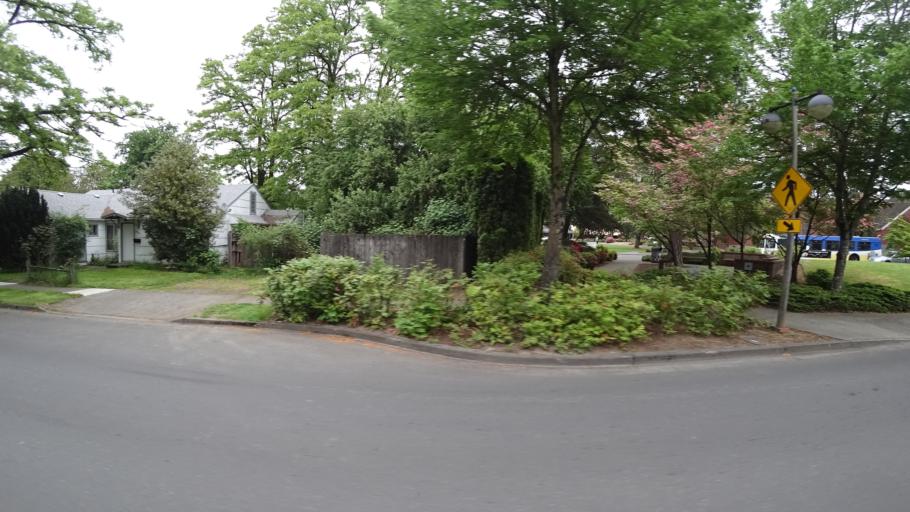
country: US
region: Oregon
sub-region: Washington County
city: Beaverton
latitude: 45.4798
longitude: -122.8062
